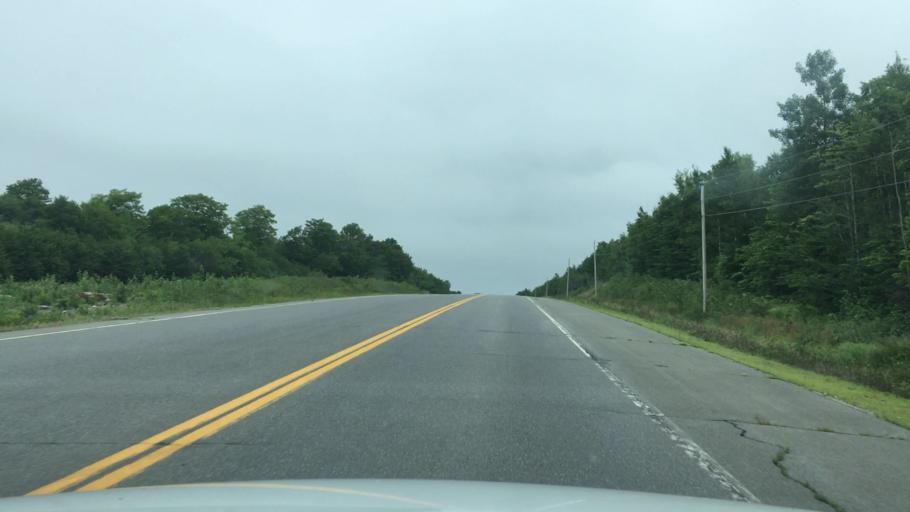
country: US
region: Maine
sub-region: Hancock County
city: Franklin
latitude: 44.8281
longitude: -68.1241
